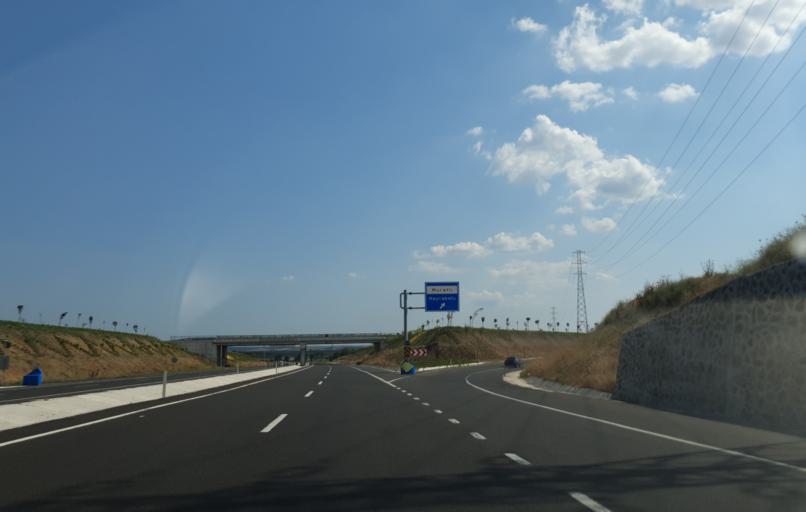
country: TR
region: Tekirdag
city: Muratli
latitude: 41.2271
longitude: 27.5323
